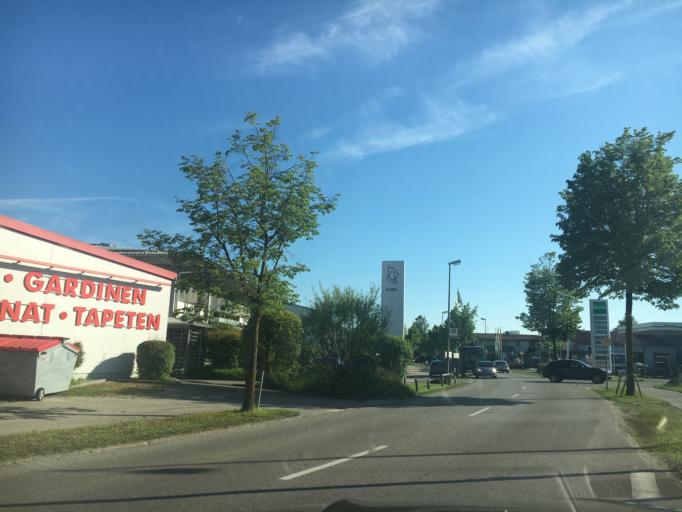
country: DE
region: Bavaria
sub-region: Upper Bavaria
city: Traunreut
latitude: 47.9618
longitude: 12.6099
